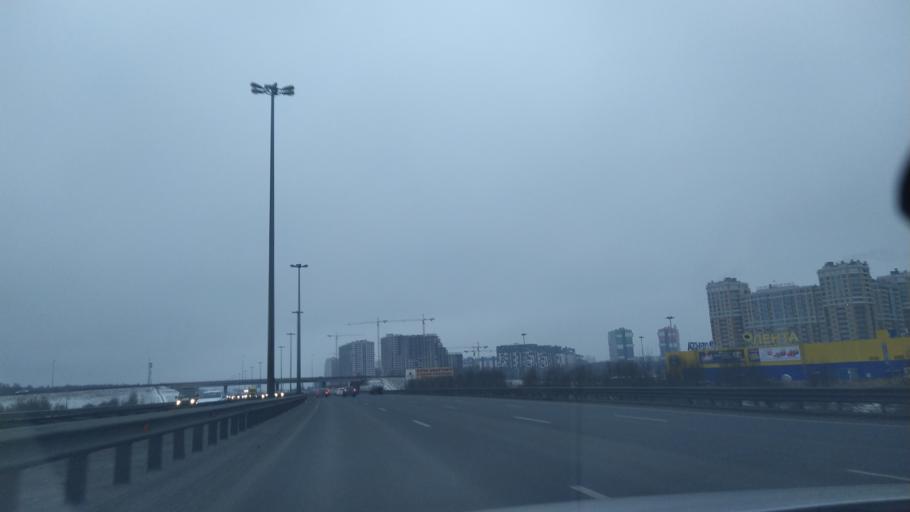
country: RU
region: St.-Petersburg
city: Krasnogvargeisky
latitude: 59.9188
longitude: 30.5258
